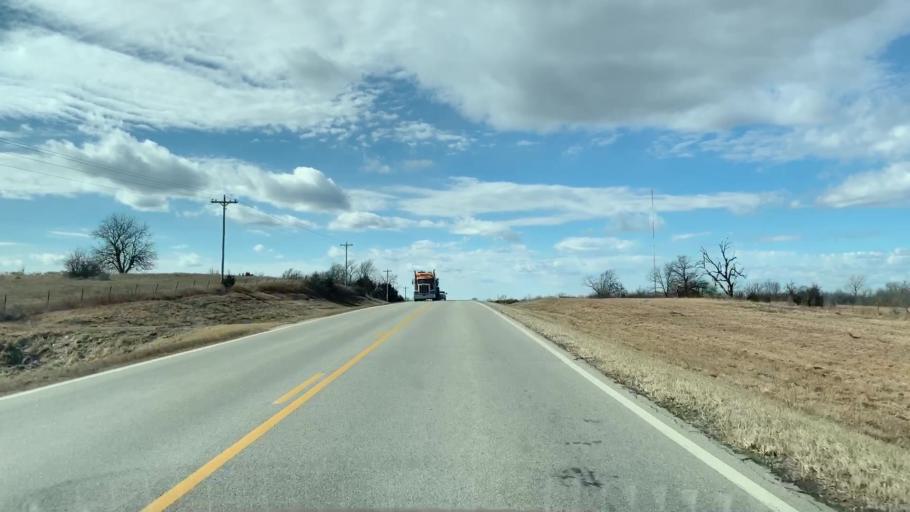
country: US
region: Kansas
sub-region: Neosho County
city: Erie
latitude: 37.5293
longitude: -95.3715
